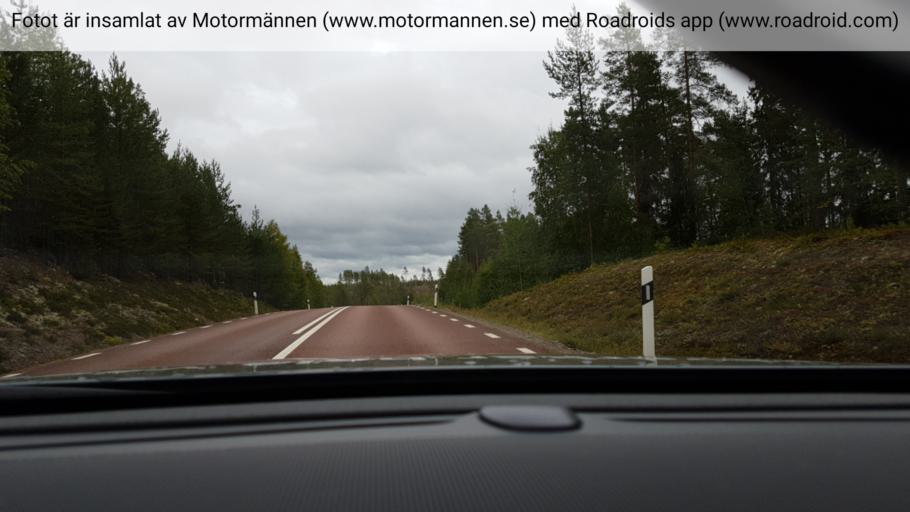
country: SE
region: Dalarna
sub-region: Malung-Saelens kommun
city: Malung
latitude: 60.8219
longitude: 13.9245
